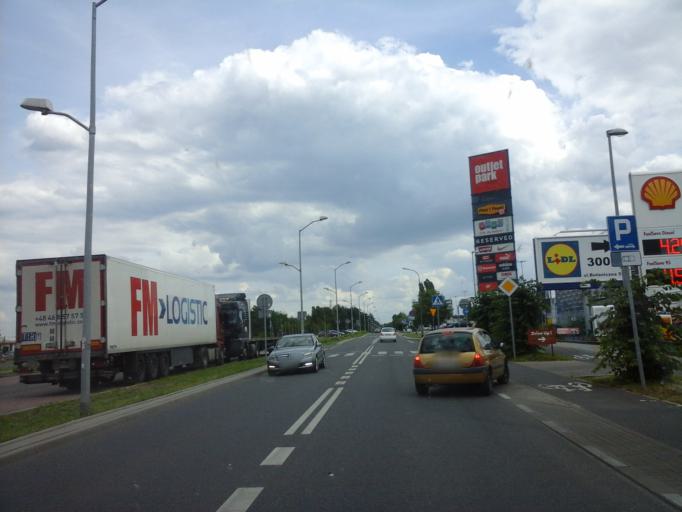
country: PL
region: West Pomeranian Voivodeship
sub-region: Szczecin
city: Szczecin
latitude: 53.3823
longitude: 14.6683
